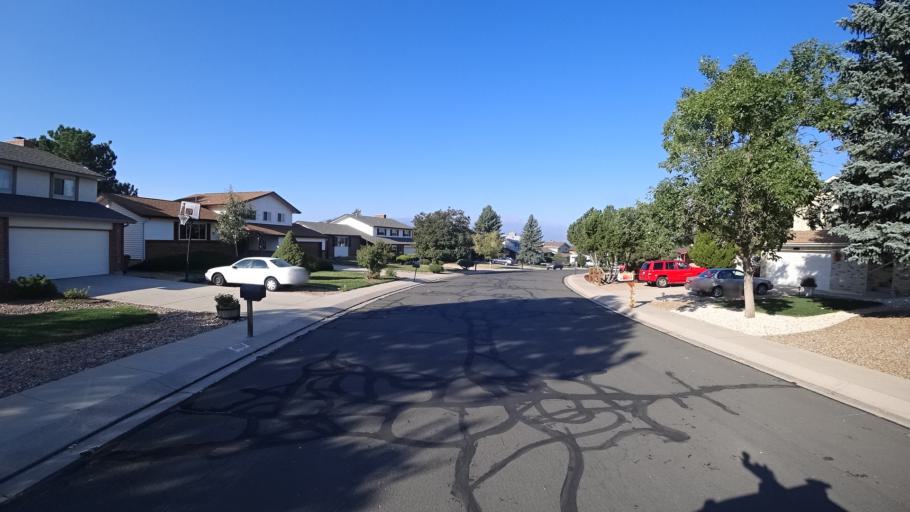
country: US
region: Colorado
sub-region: El Paso County
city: Cimarron Hills
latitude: 38.8873
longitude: -104.7312
